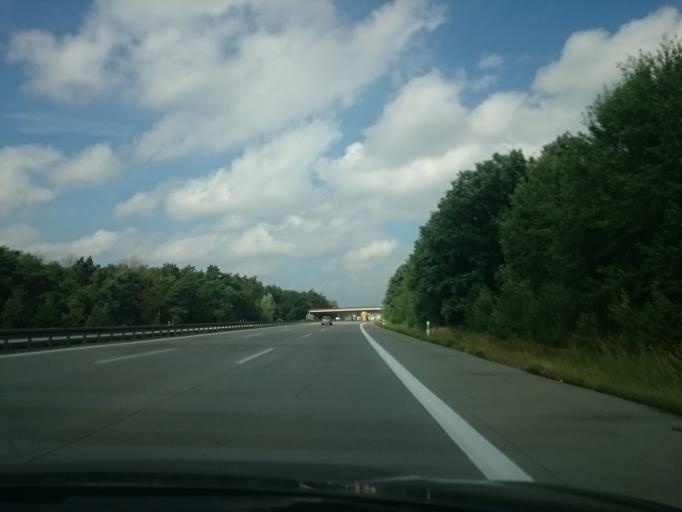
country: DE
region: Brandenburg
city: Hoppegarten
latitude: 52.5671
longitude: 13.6499
